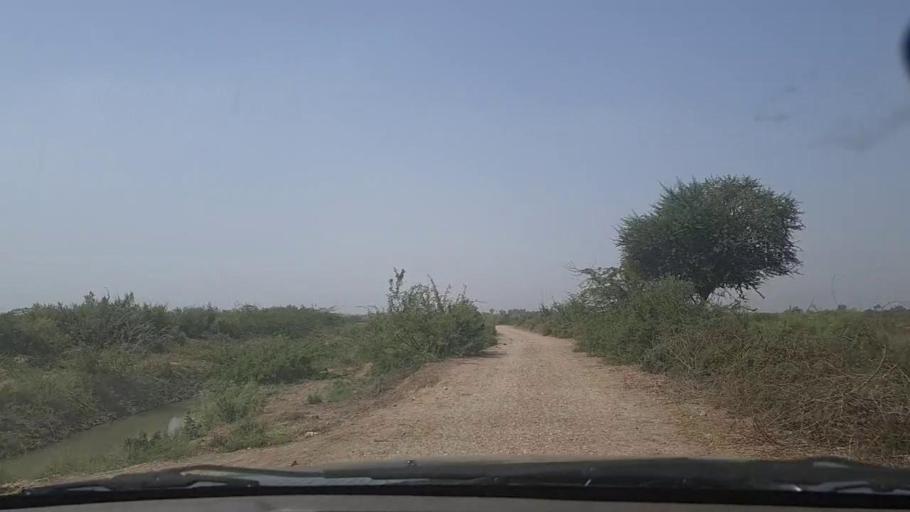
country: PK
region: Sindh
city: Keti Bandar
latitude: 24.2636
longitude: 67.6580
